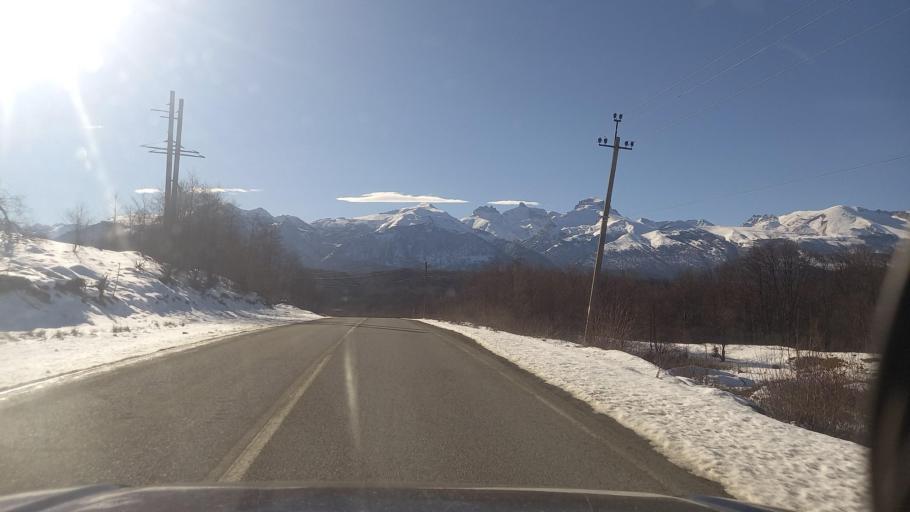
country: RU
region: North Ossetia
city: Chikola
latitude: 43.1230
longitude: 43.8154
